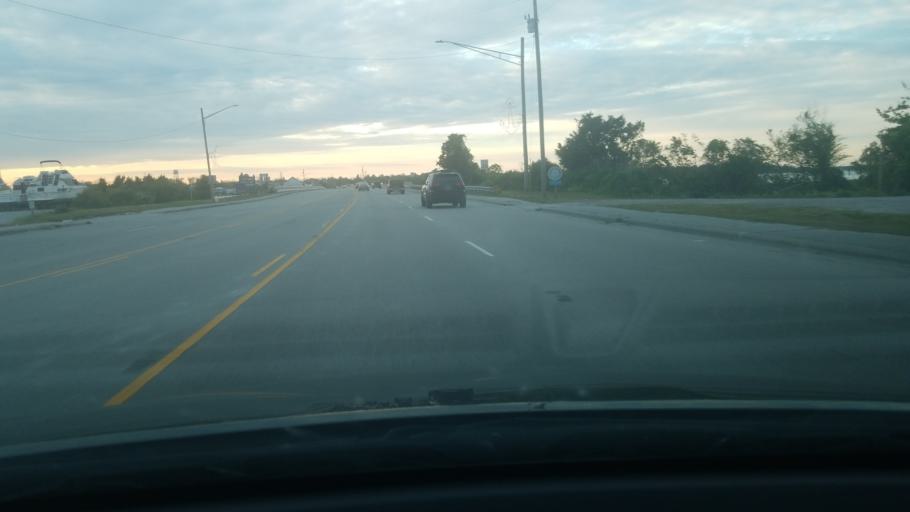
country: US
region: North Carolina
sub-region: Onslow County
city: Swansboro
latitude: 34.6812
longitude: -77.1112
